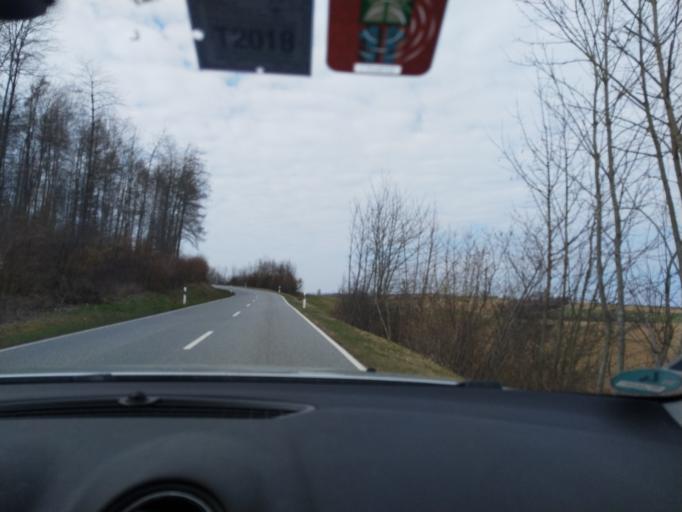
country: DE
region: Baden-Wuerttemberg
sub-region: Regierungsbezirk Stuttgart
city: Ilsfeld
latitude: 49.0408
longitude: 9.2230
